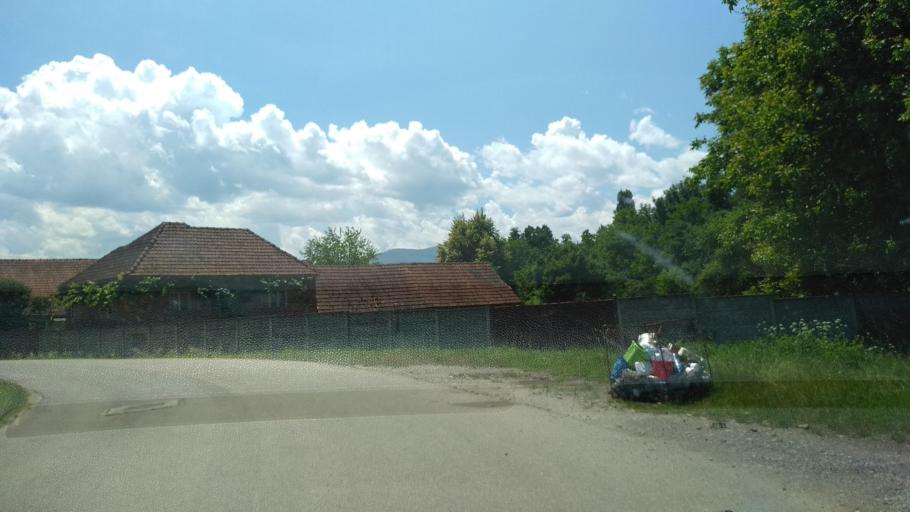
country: RO
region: Hunedoara
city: Densus
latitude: 45.5522
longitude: 22.8225
